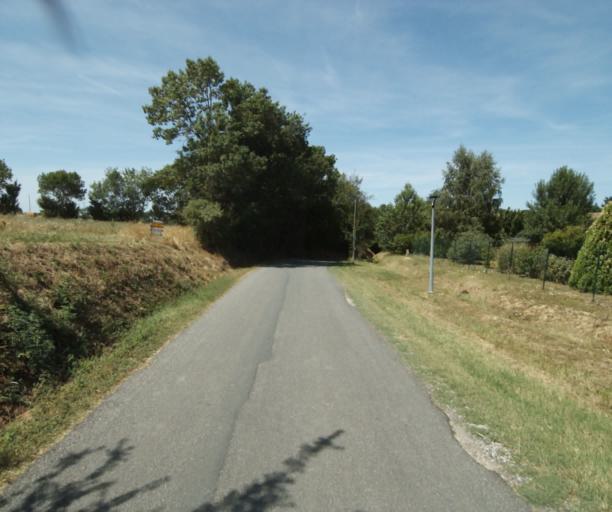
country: FR
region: Midi-Pyrenees
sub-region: Departement de la Haute-Garonne
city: Revel
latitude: 43.4937
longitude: 2.0218
